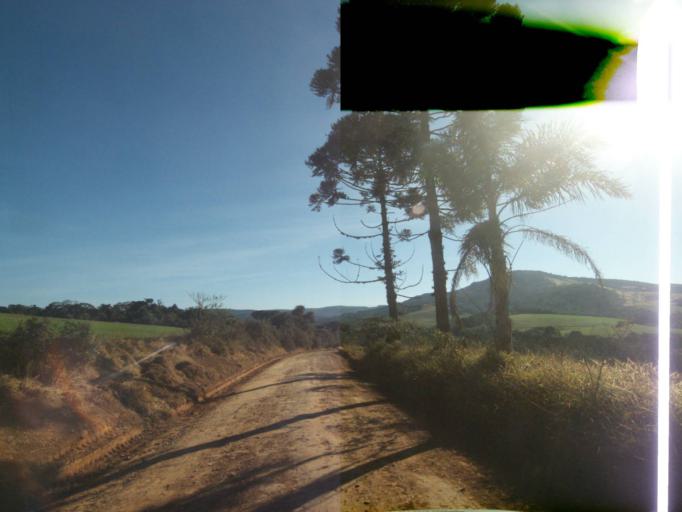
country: BR
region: Parana
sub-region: Tibagi
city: Tibagi
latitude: -24.5229
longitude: -50.5005
